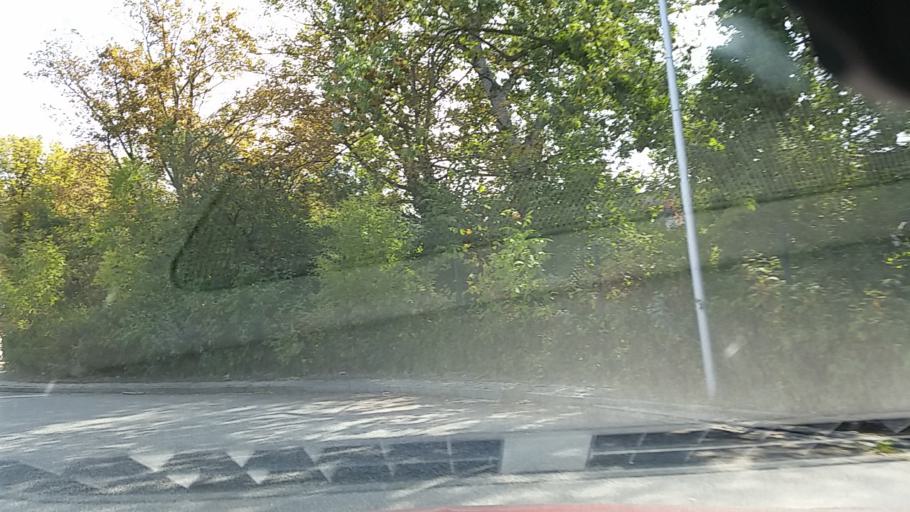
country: DE
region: Thuringia
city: Artern
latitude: 51.3626
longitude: 11.3058
